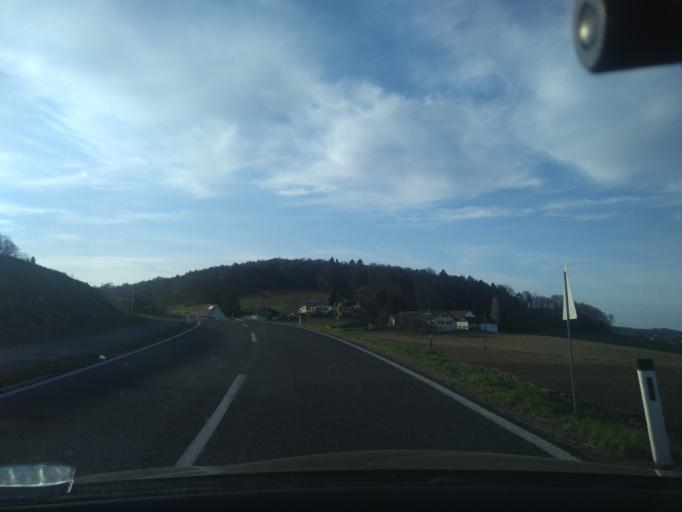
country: AT
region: Styria
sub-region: Politischer Bezirk Suedoststeiermark
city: Sankt Stefan im Rosental
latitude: 46.8820
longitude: 15.7211
